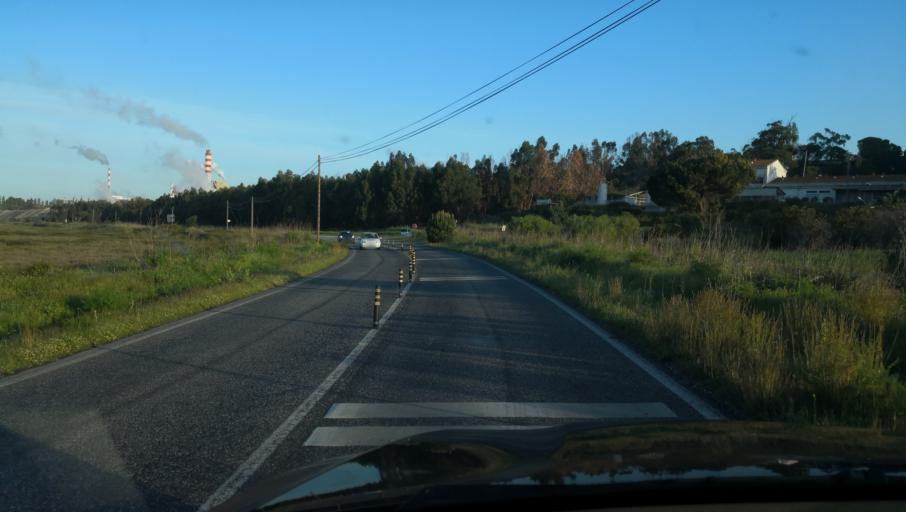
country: PT
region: Setubal
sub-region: Setubal
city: Setubal
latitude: 38.4895
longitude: -8.7943
